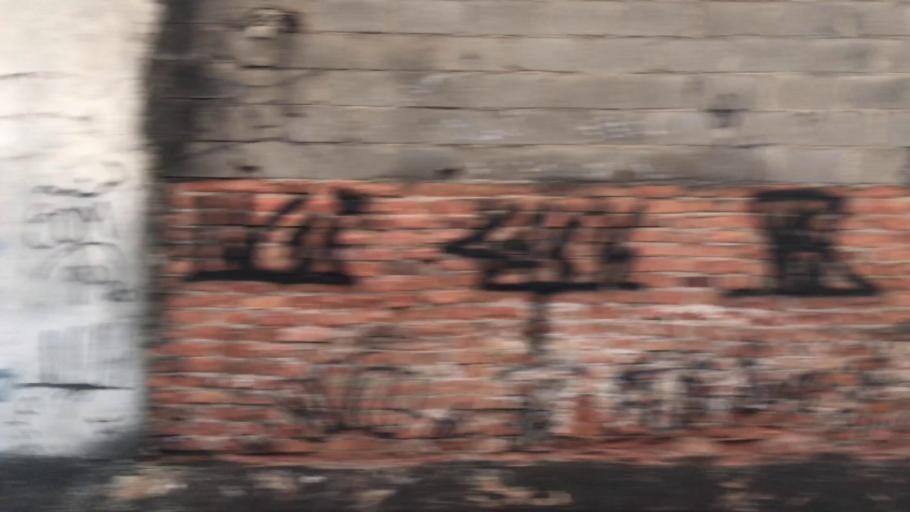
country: BR
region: Rio de Janeiro
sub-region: Rio De Janeiro
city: Rio de Janeiro
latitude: -22.9014
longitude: -43.2543
